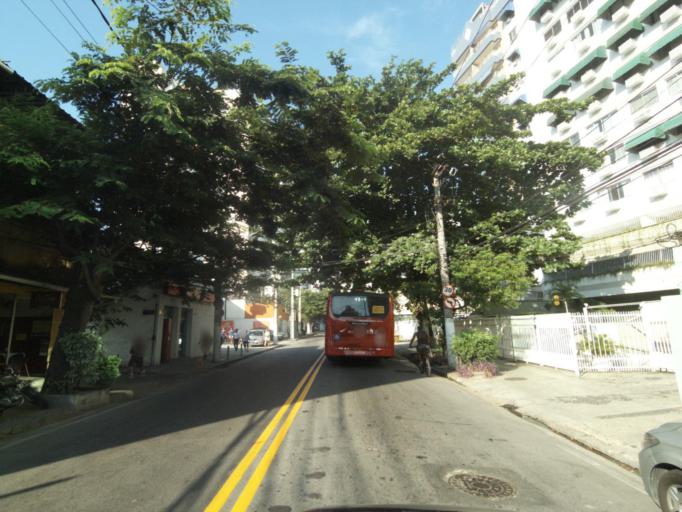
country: BR
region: Rio de Janeiro
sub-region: Niteroi
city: Niteroi
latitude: -22.8979
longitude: -43.1028
